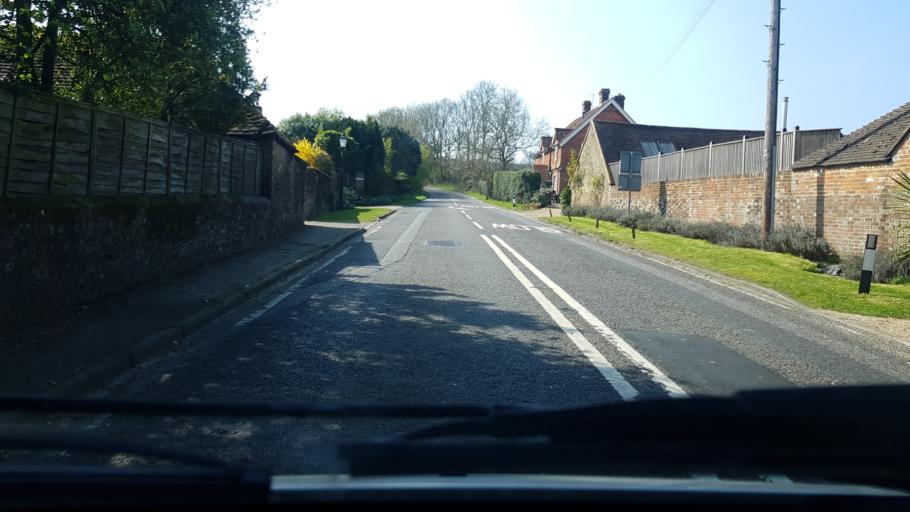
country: GB
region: England
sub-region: West Sussex
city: Fernhurst
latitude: 51.0380
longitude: -0.7235
